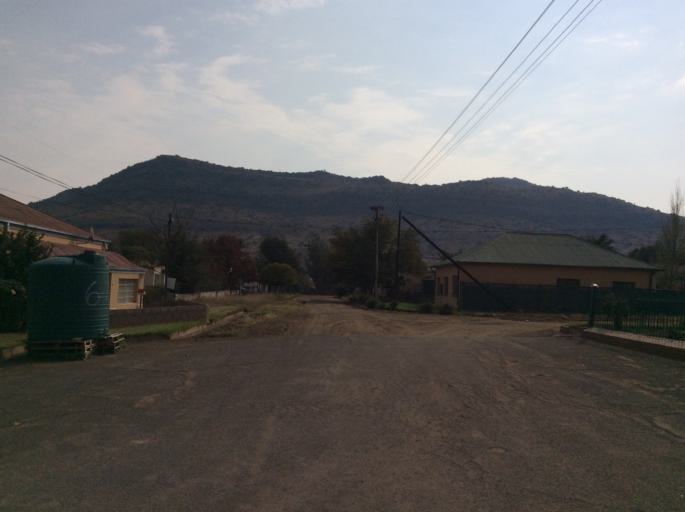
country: LS
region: Mafeteng
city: Mafeteng
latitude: -29.7275
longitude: 27.0438
